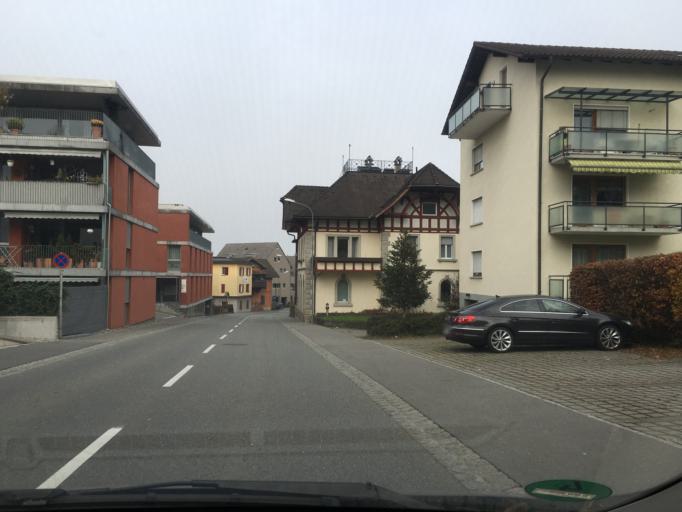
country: AT
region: Vorarlberg
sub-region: Politischer Bezirk Feldkirch
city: Gotzis
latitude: 47.3341
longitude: 9.6480
